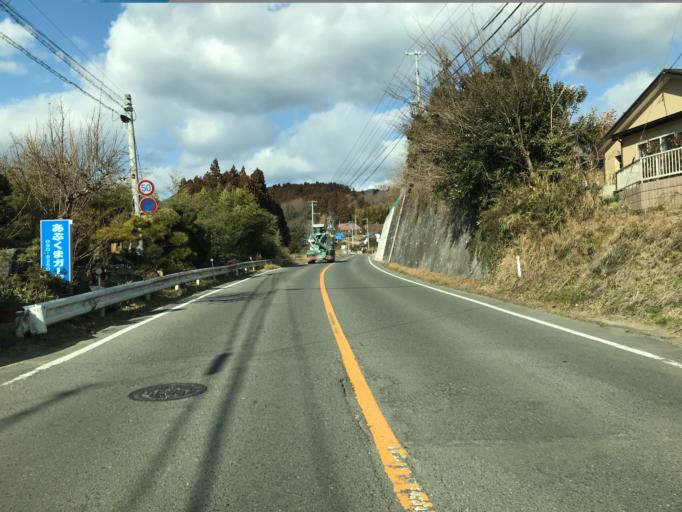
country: JP
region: Fukushima
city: Iwaki
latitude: 37.1201
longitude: 140.8714
